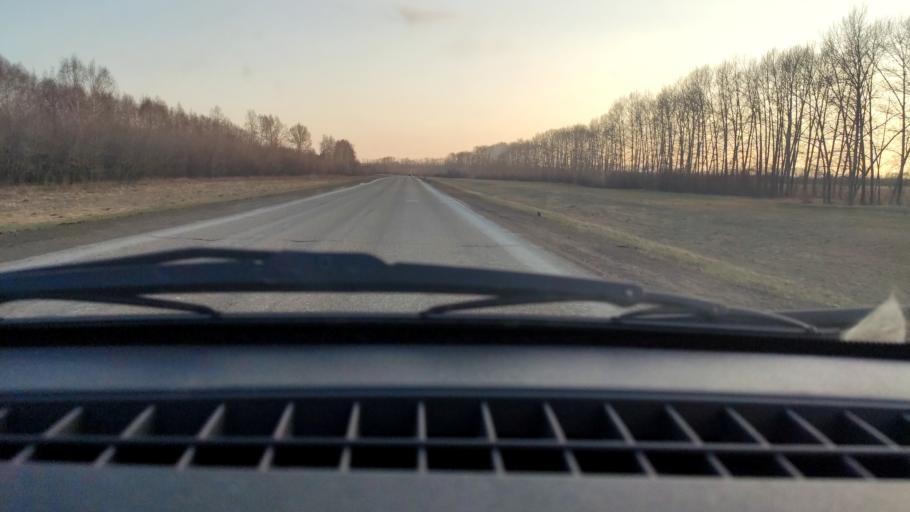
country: RU
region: Bashkortostan
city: Davlekanovo
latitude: 54.3544
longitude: 55.1853
